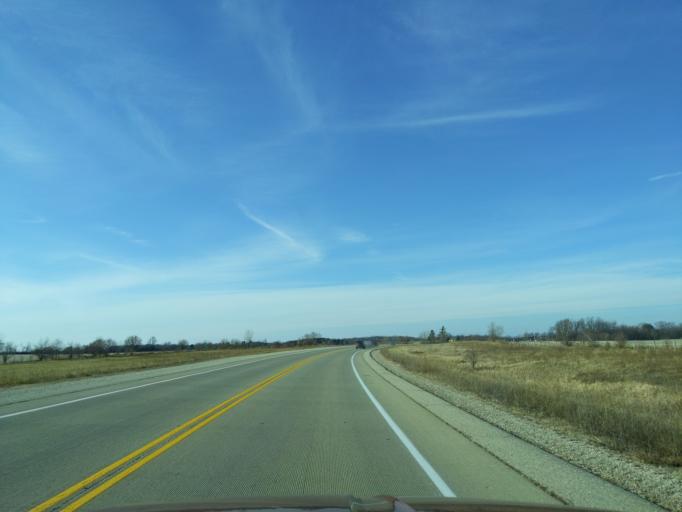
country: US
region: Wisconsin
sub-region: Walworth County
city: Whitewater
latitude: 42.8226
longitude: -88.7642
